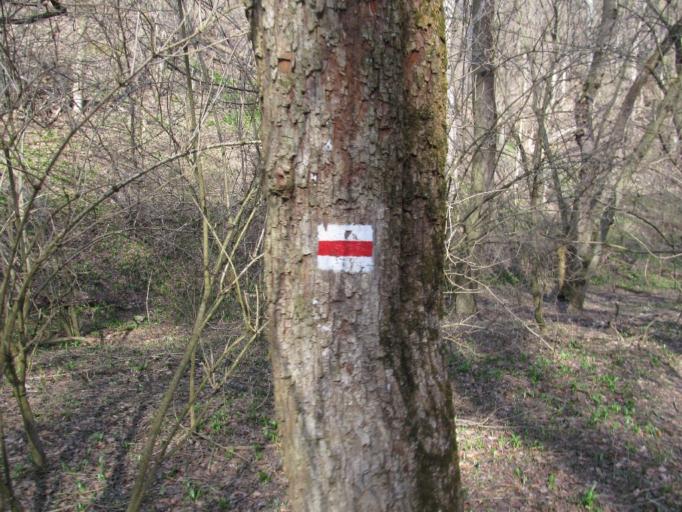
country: HU
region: Veszprem
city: Varpalota
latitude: 47.2724
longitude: 18.1608
